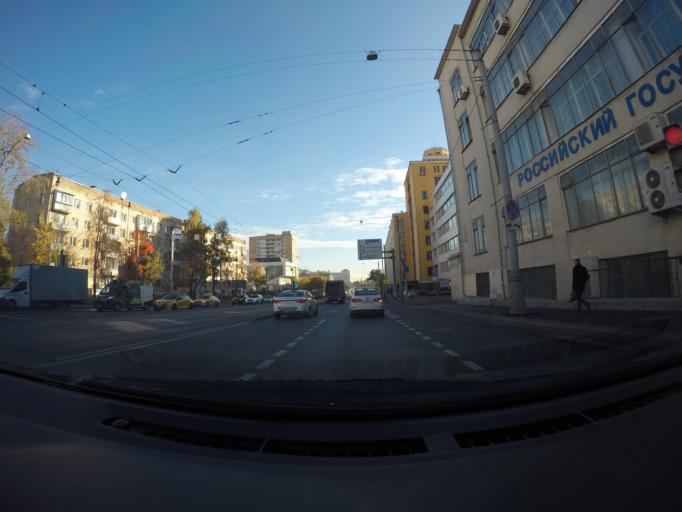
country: RU
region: Moscow
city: Sokol'niki
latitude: 55.7932
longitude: 37.6955
